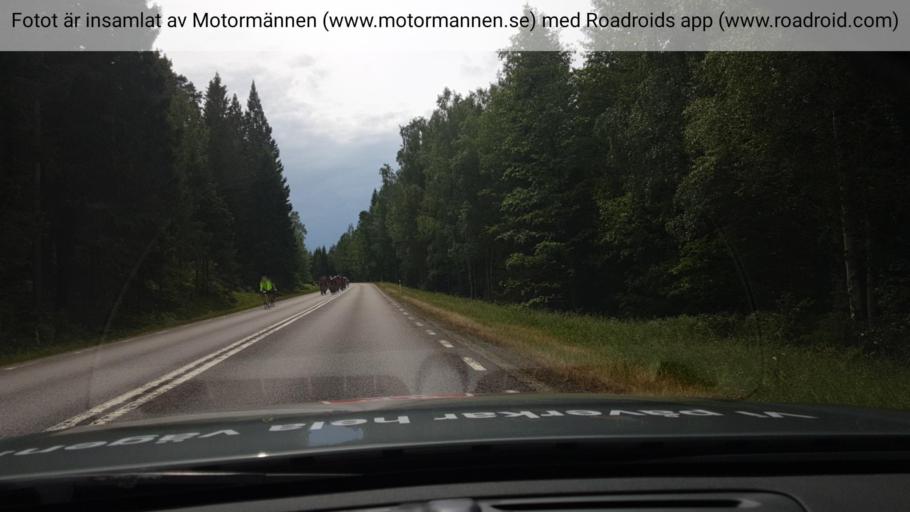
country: SE
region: OErebro
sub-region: Askersunds Kommun
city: Askersund
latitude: 58.7621
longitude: 14.7957
